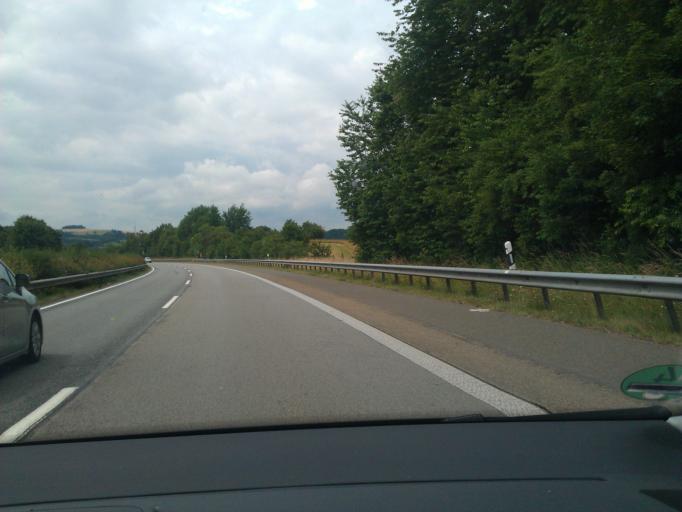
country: DE
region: Rheinland-Pfalz
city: Niedermohr
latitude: 49.4525
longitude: 7.4786
